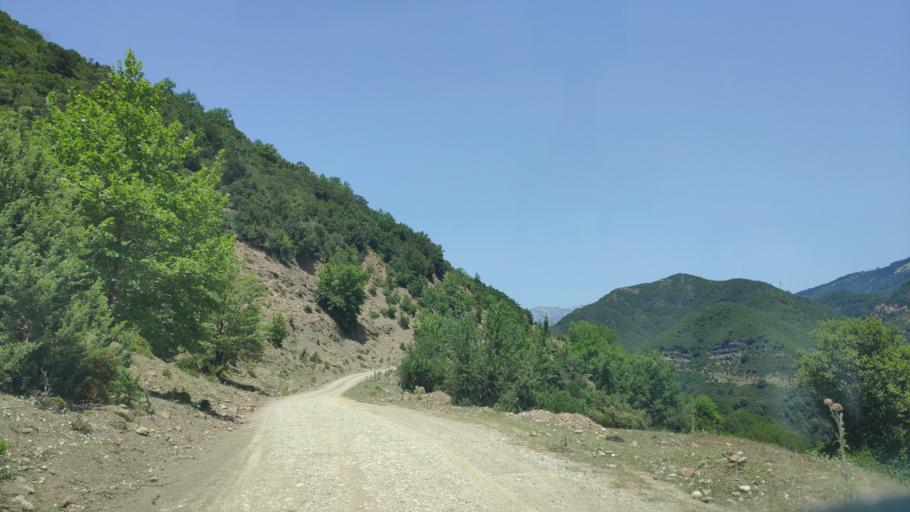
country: GR
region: Thessaly
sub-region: Nomos Kardhitsas
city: Anthiro
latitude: 39.1726
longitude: 21.3704
